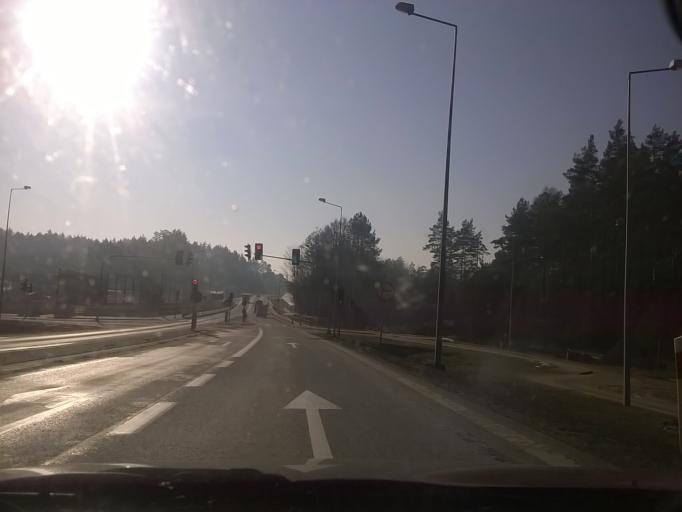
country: PL
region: Warmian-Masurian Voivodeship
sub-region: Powiat olsztynski
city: Barczewo
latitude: 53.8040
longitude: 20.6221
